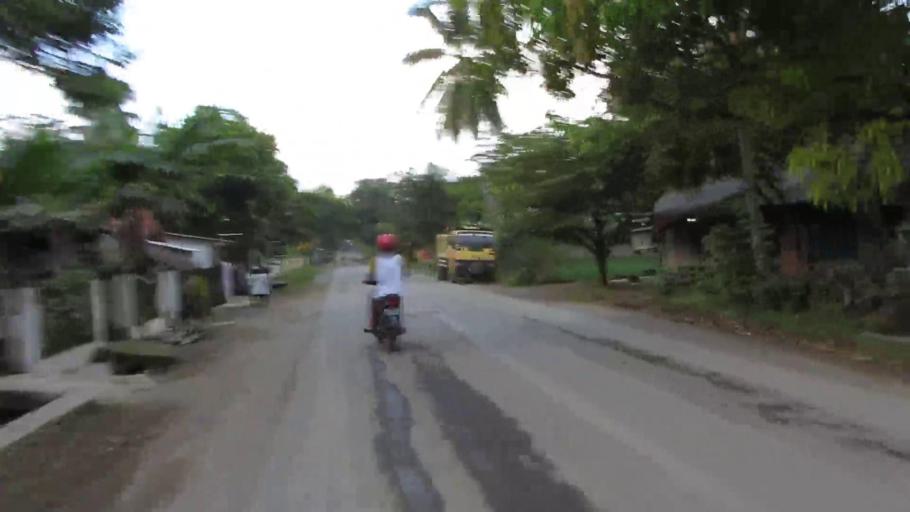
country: ID
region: West Java
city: Binangun
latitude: -7.7172
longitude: 108.4760
